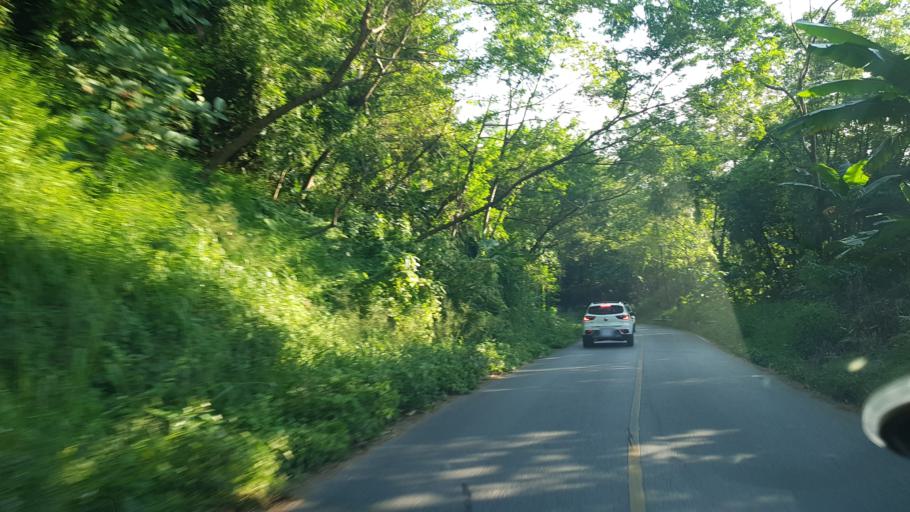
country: TH
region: Chiang Rai
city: Mae Fa Luang
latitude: 20.3163
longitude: 99.8179
